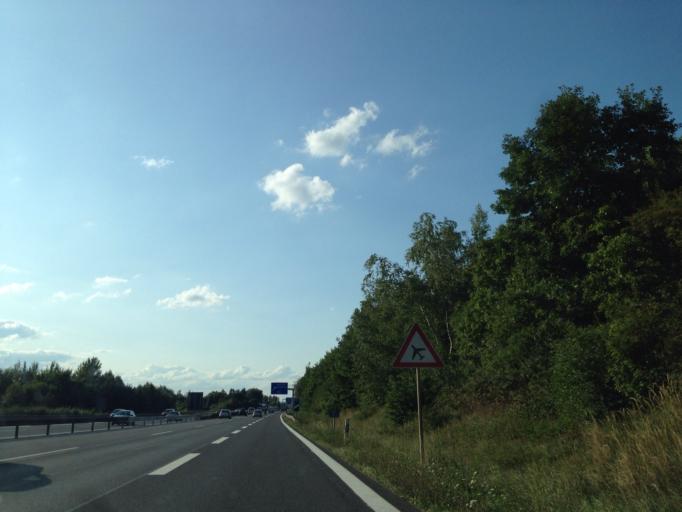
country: DE
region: Bavaria
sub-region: Upper Franconia
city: Gundelsheim
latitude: 49.9241
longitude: 10.9238
